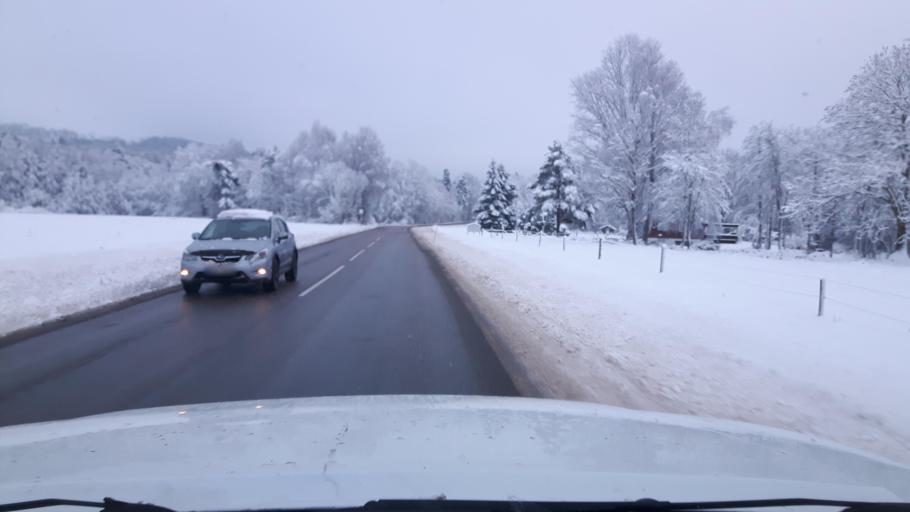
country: SE
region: Halland
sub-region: Kungsbacka Kommun
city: Fjaeras kyrkby
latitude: 57.4183
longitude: 12.2070
